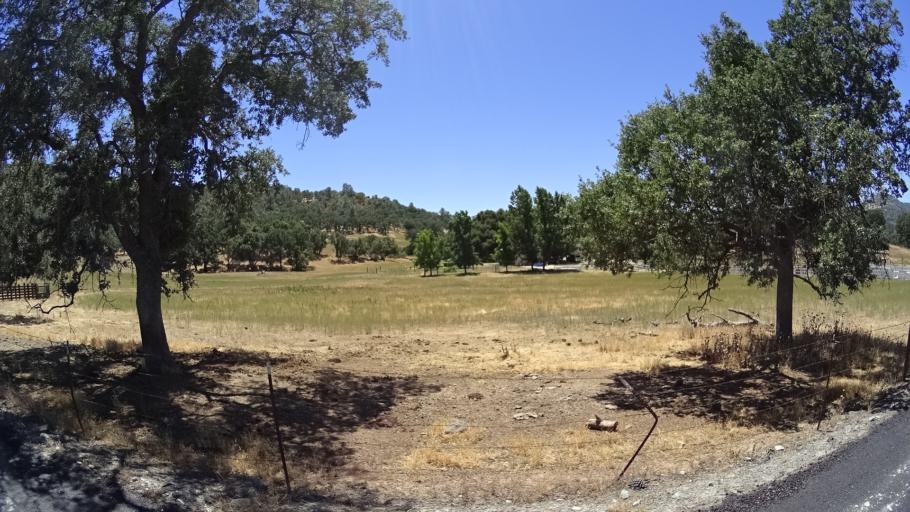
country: US
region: California
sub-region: Calaveras County
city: Copperopolis
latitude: 38.0531
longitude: -120.6204
